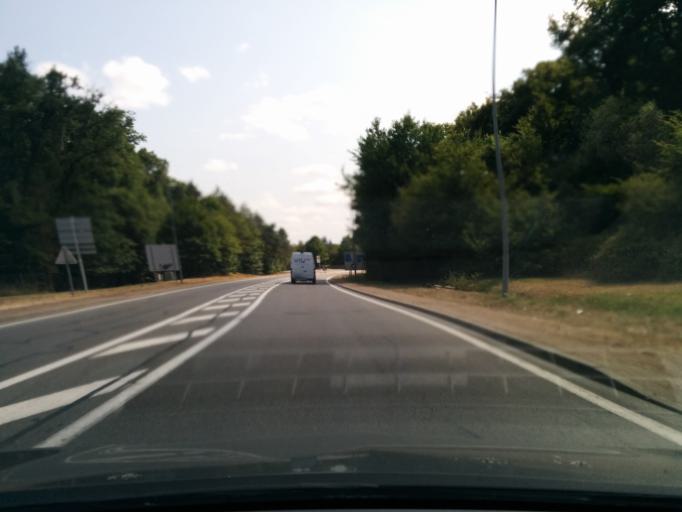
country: FR
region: Centre
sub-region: Departement du Cher
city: Vierzon
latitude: 47.2482
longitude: 2.0605
